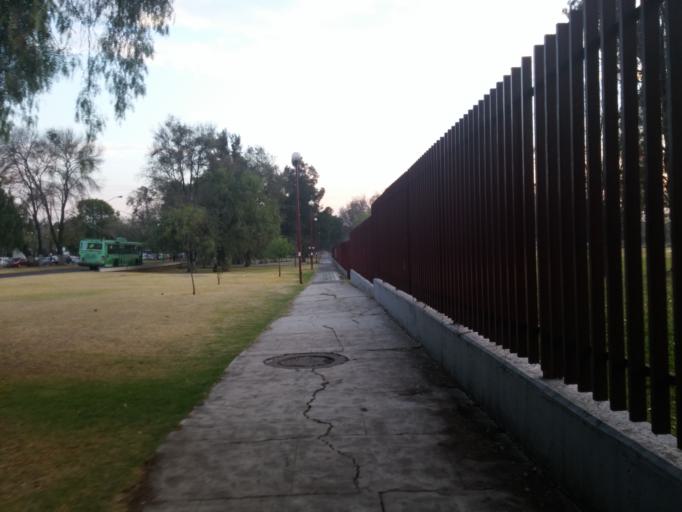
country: MX
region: Mexico
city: Colonia Lindavista
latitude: 19.5032
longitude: -99.1360
